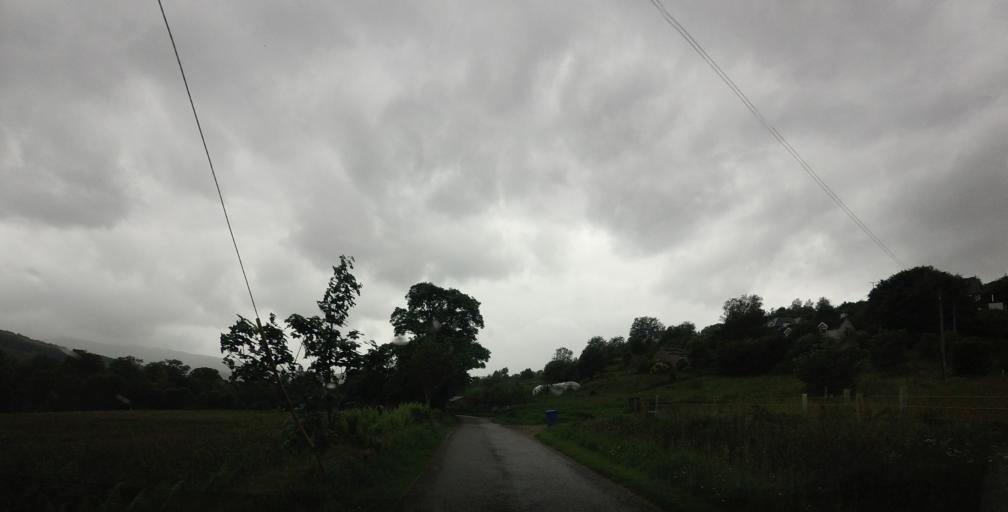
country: GB
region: Scotland
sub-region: Argyll and Bute
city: Oban
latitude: 56.7043
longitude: -5.5698
